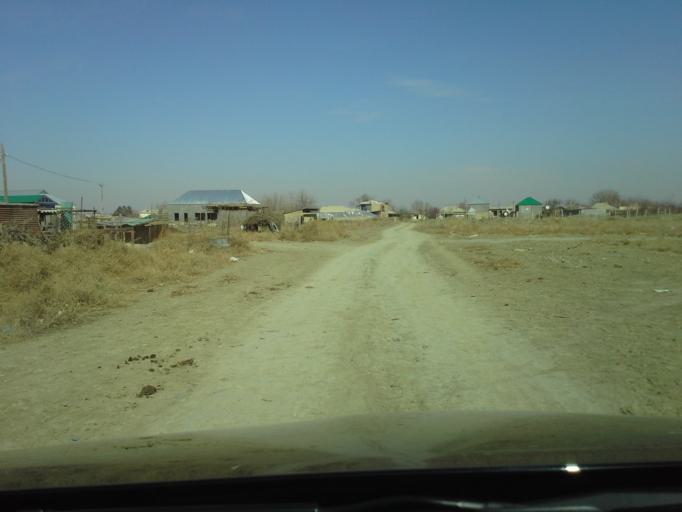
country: TM
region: Ahal
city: Abadan
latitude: 38.1022
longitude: 58.0331
